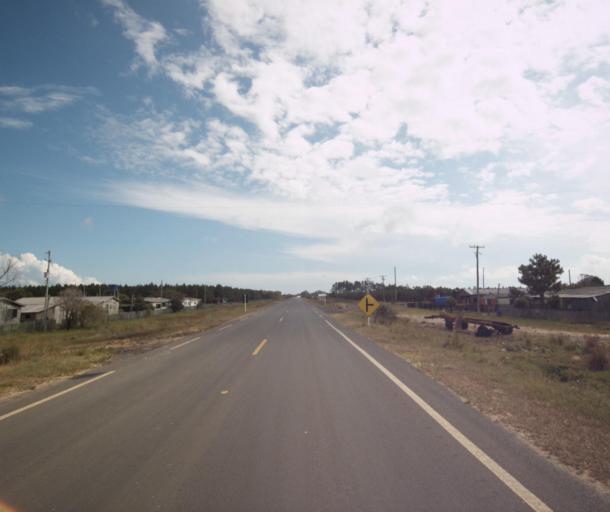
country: BR
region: Rio Grande do Sul
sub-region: Sao Lourenco Do Sul
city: Sao Lourenco do Sul
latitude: -31.6023
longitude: -51.3816
